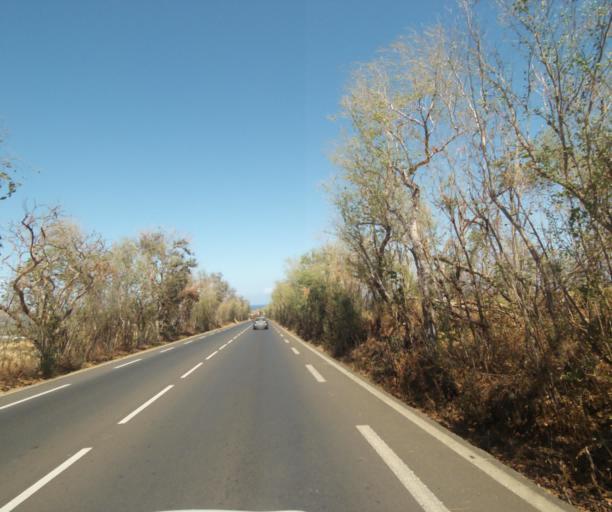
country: RE
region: Reunion
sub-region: Reunion
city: Saint-Paul
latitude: -20.9821
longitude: 55.3076
